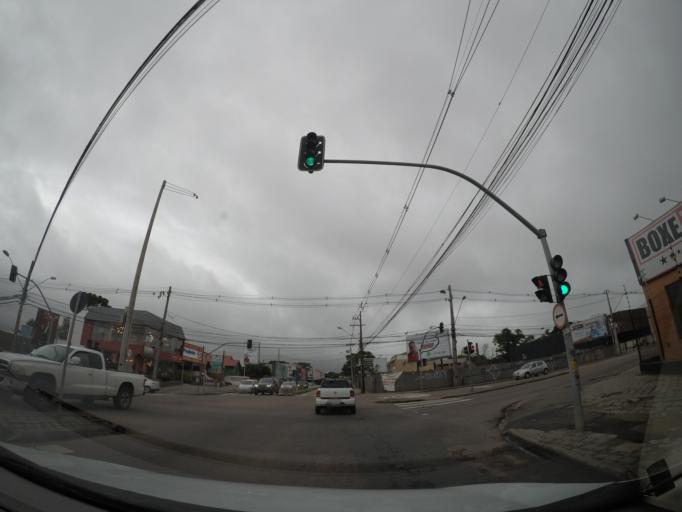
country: BR
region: Parana
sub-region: Curitiba
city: Curitiba
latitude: -25.4493
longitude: -49.3044
